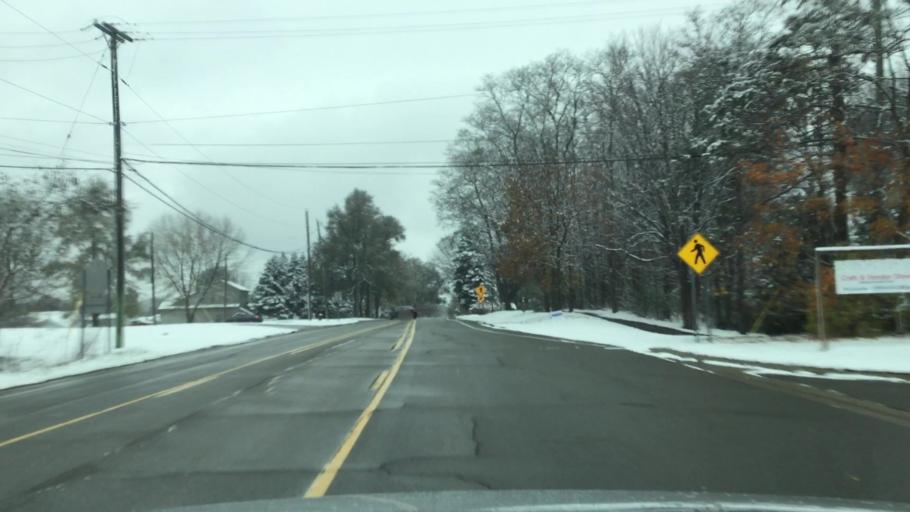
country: US
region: Michigan
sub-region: Oakland County
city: Oxford
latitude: 42.8095
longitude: -83.2859
